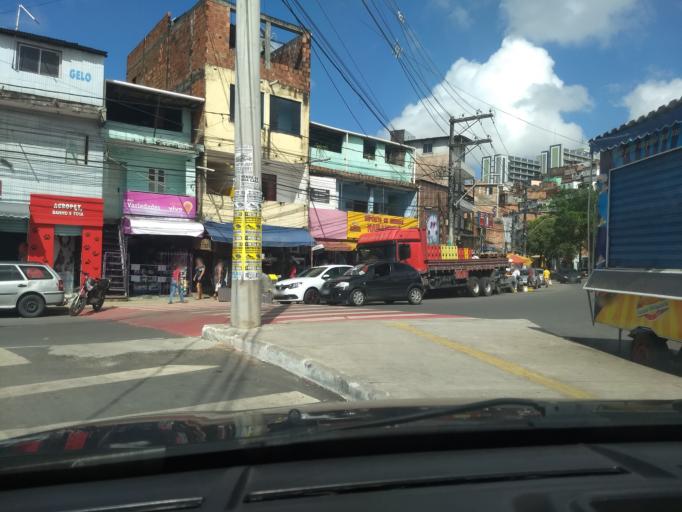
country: BR
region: Bahia
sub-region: Salvador
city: Salvador
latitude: -12.9534
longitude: -38.4474
